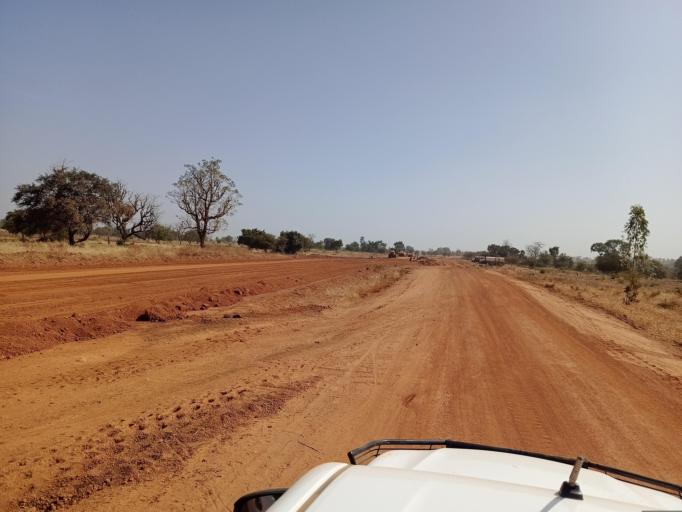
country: BF
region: Centre-Est
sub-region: Province du Boulgou
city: Garango
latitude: 11.5020
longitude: -0.5017
